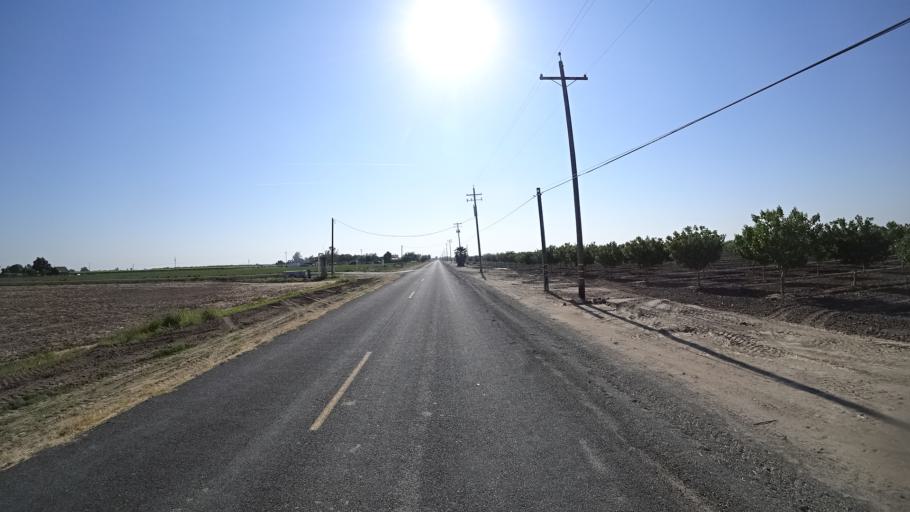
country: US
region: California
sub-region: Fresno County
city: Riverdale
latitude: 36.3657
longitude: -119.8723
